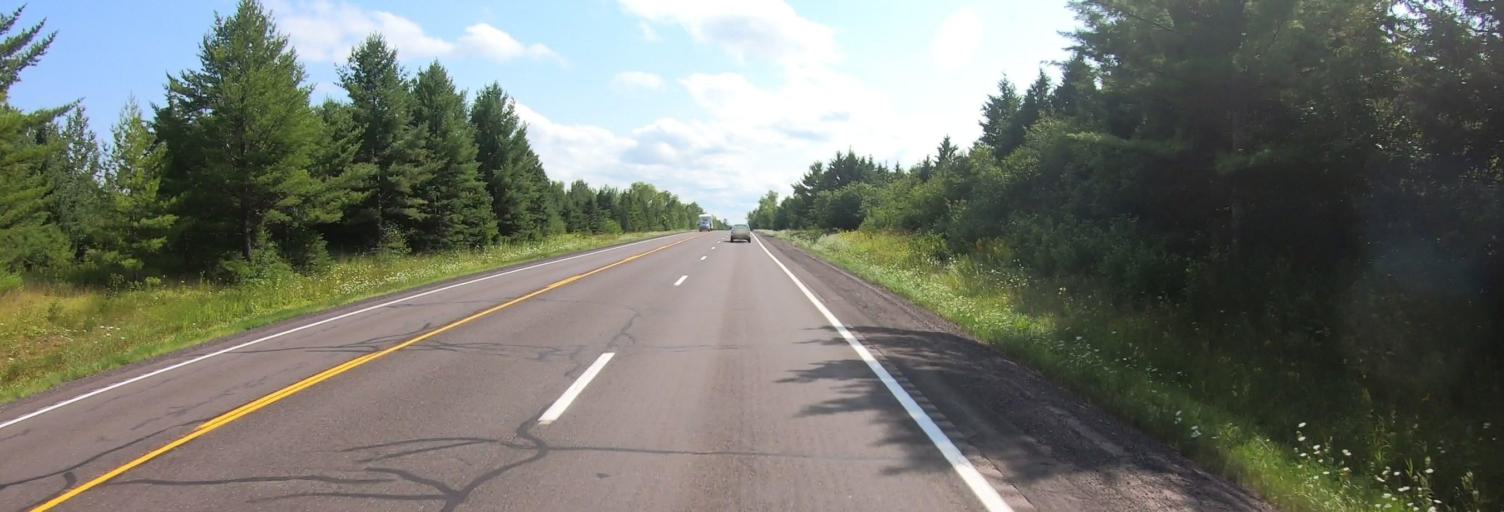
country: US
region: Michigan
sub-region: Ontonagon County
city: Ontonagon
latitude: 46.6716
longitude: -89.1686
